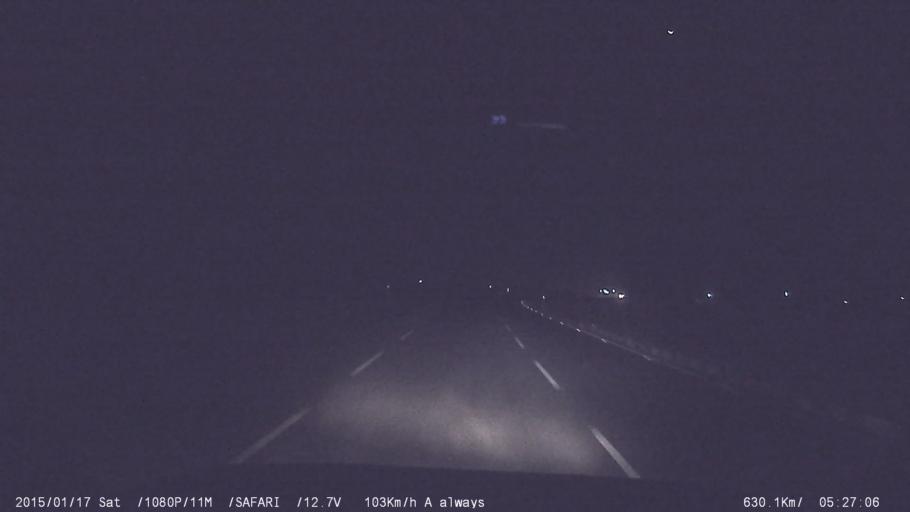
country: IN
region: Tamil Nadu
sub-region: Vellore
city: Arcot
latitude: 12.9357
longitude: 79.2561
